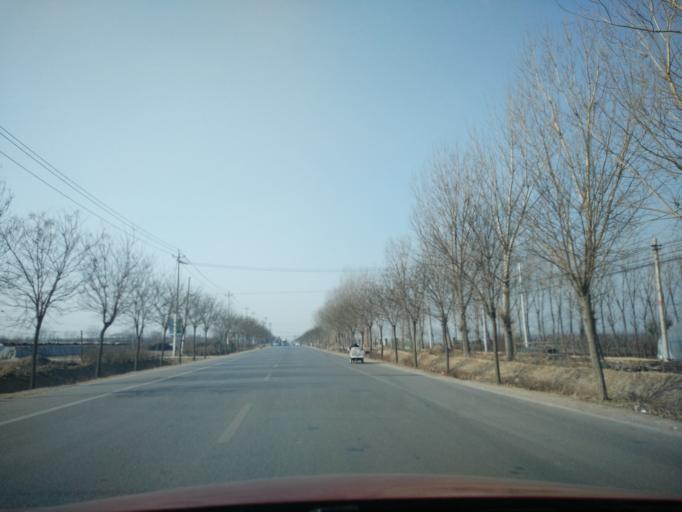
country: CN
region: Beijing
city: Yinghai
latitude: 39.7057
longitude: 116.4394
